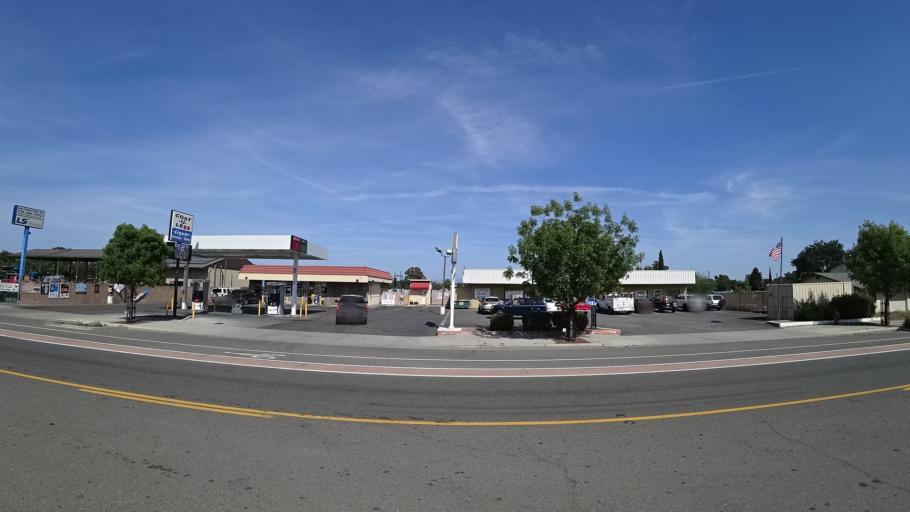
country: US
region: California
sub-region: Tehama County
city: Los Molinos
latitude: 40.0268
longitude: -122.0999
